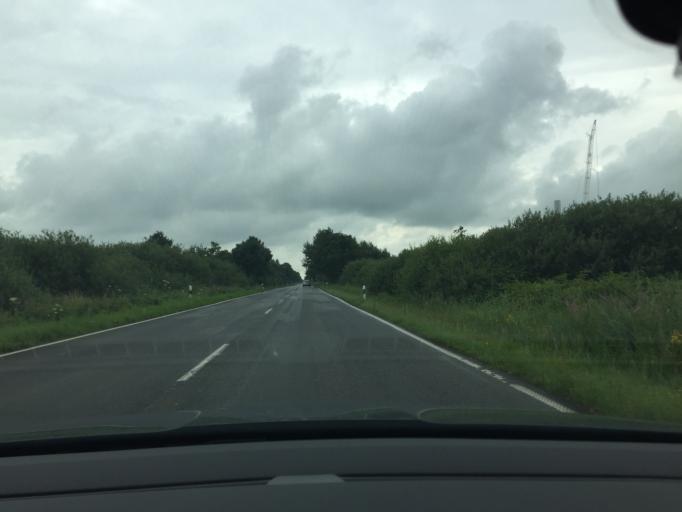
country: DE
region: Lower Saxony
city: Jemgum
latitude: 53.3628
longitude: 7.3469
